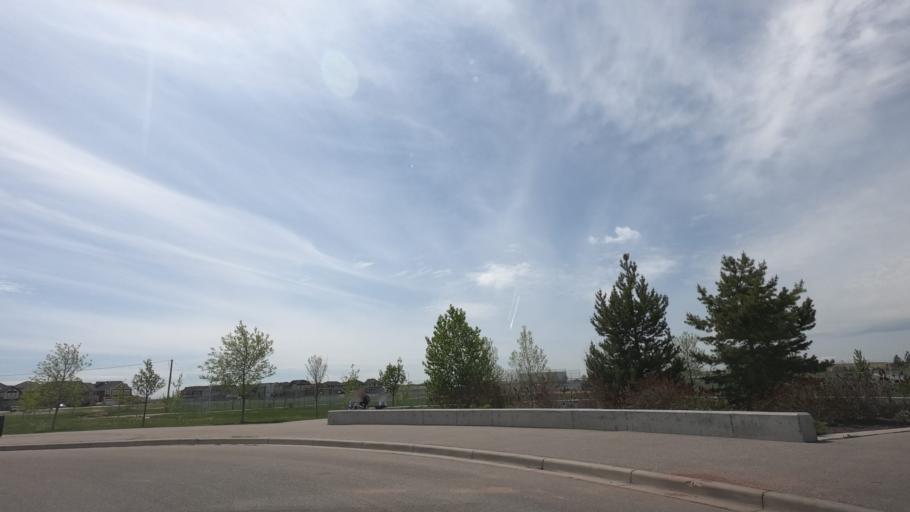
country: CA
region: Alberta
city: Airdrie
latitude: 51.2653
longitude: -114.0329
